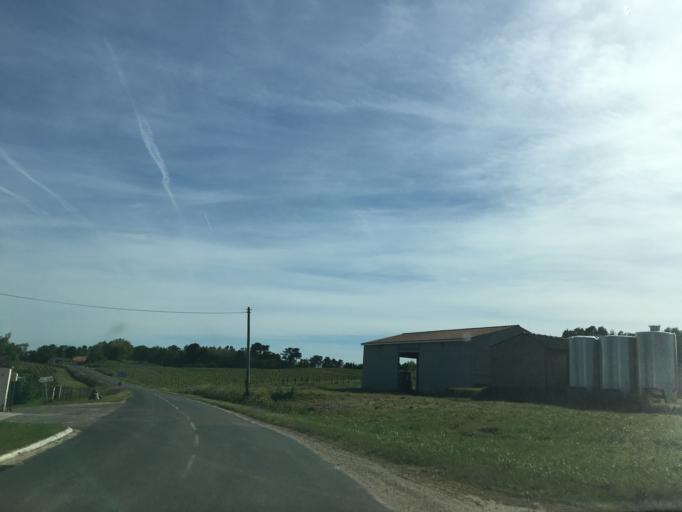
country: FR
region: Poitou-Charentes
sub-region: Departement de la Charente-Maritime
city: Mirambeau
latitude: 45.3348
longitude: -0.5937
